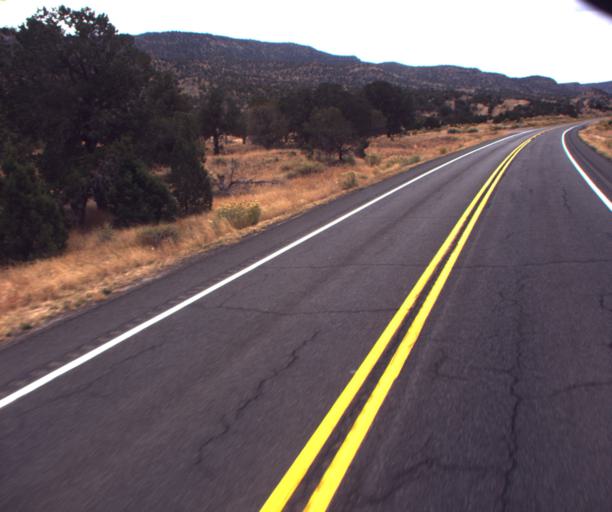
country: US
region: Arizona
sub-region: Navajo County
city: Kayenta
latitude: 36.6420
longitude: -110.4371
